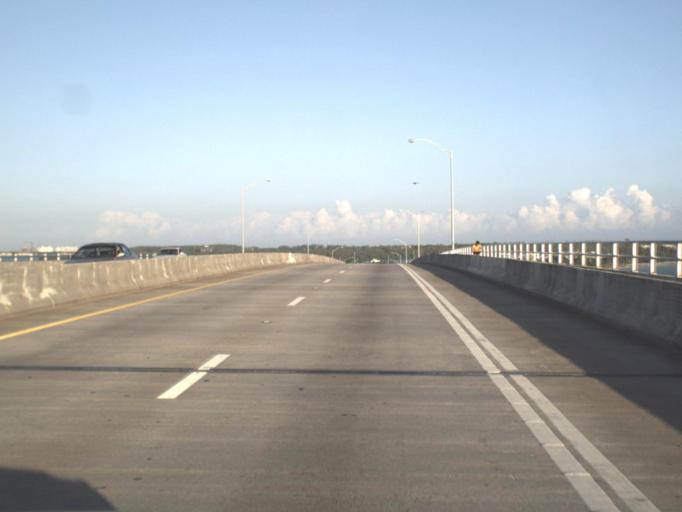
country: US
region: Florida
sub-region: Miami-Dade County
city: Miami
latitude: 25.7464
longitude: -80.1850
